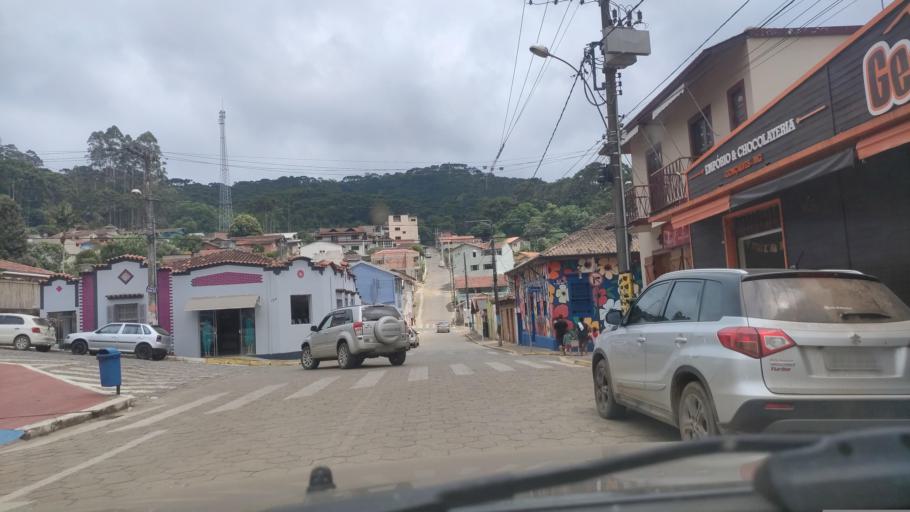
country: BR
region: Minas Gerais
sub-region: Paraisopolis
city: Paraisopolis
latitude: -22.6590
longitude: -45.8560
